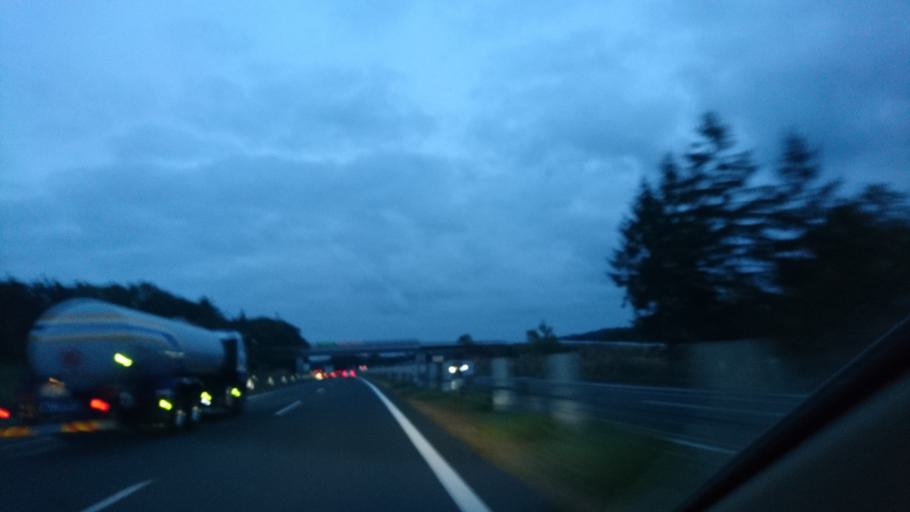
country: JP
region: Iwate
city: Hanamaki
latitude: 39.5106
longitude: 141.1018
